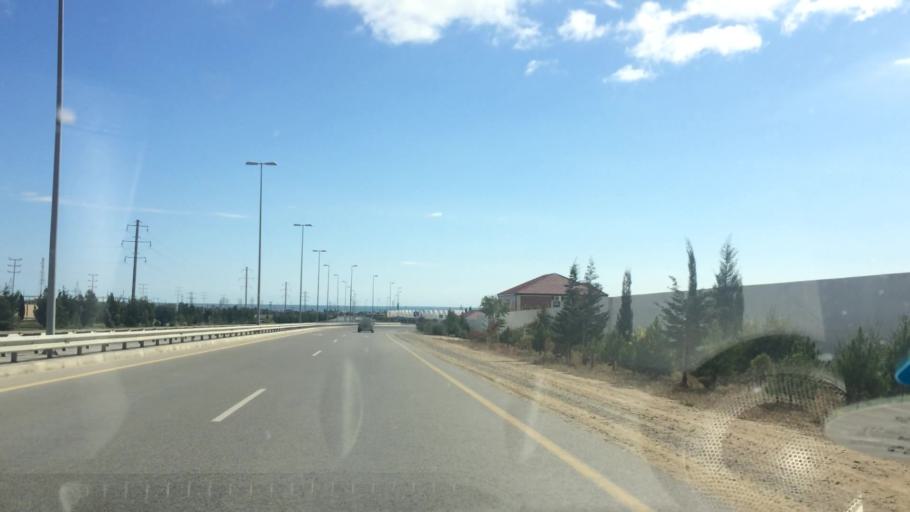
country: AZ
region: Baki
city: Zyrya
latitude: 40.3998
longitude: 50.3173
